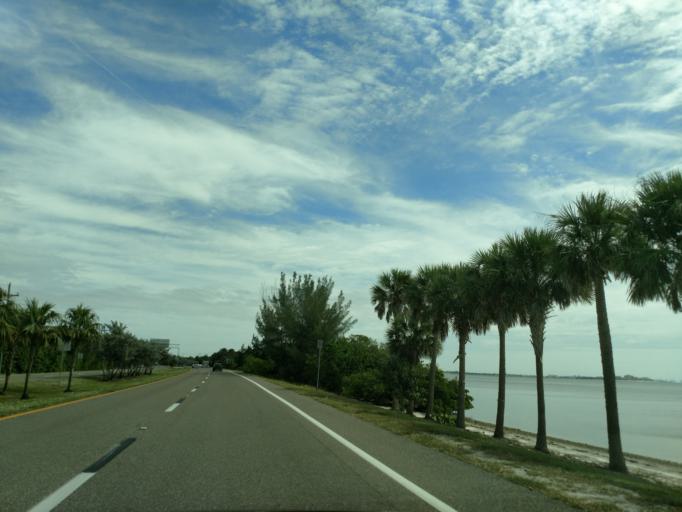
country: US
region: Florida
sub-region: Lee County
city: Punta Rassa
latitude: 26.4851
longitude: -82.0013
